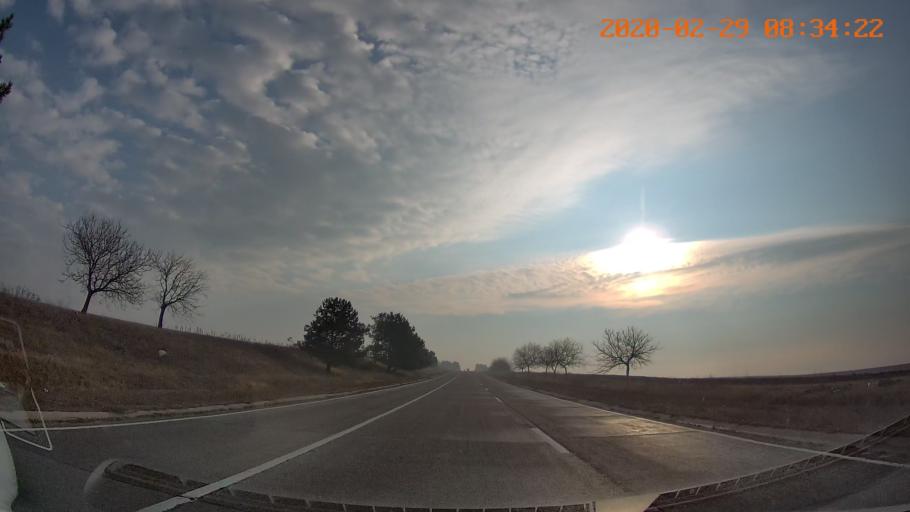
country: MD
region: Anenii Noi
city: Anenii Noi
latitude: 46.9251
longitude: 29.3078
